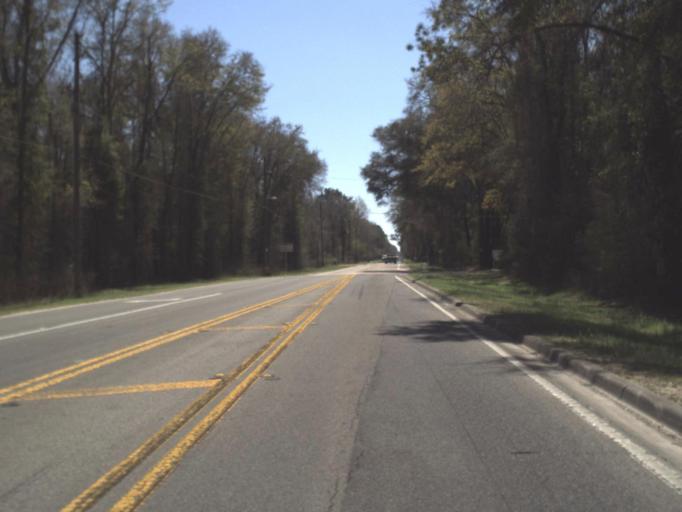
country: US
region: Florida
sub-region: Leon County
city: Woodville
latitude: 30.2684
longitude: -84.2378
